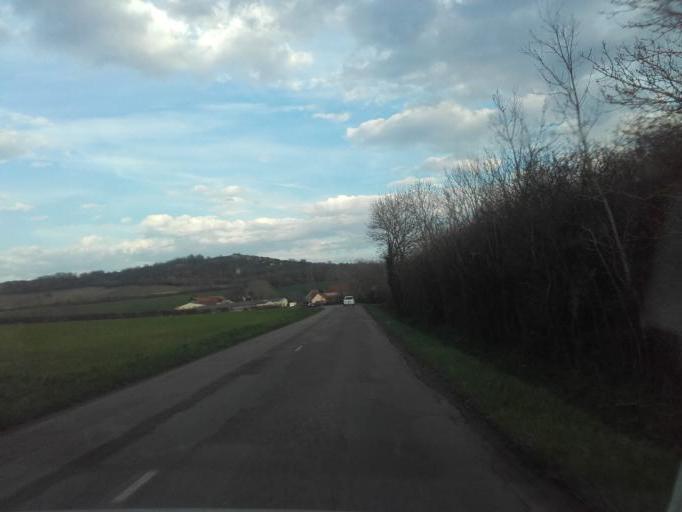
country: FR
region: Bourgogne
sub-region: Departement de la Cote-d'Or
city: Nolay
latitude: 46.9422
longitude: 4.6572
